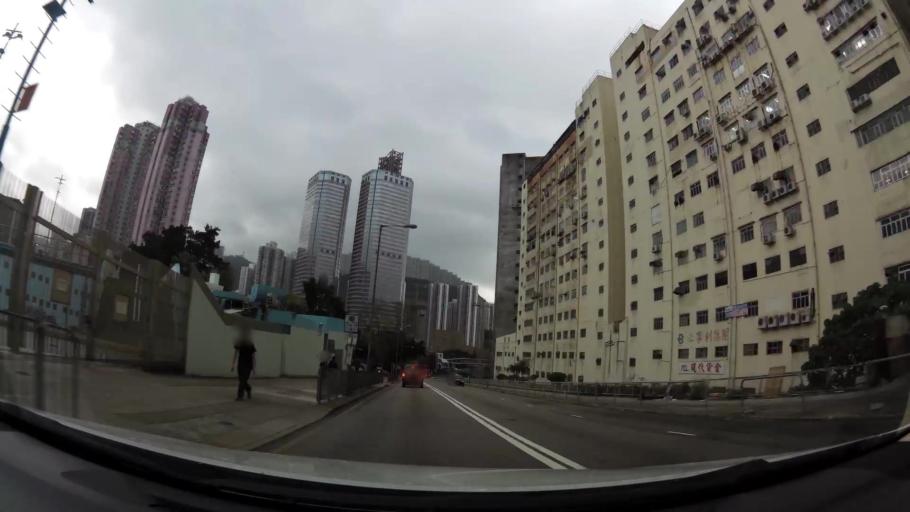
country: HK
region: Tsuen Wan
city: Tsuen Wan
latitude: 22.3585
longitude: 114.1228
